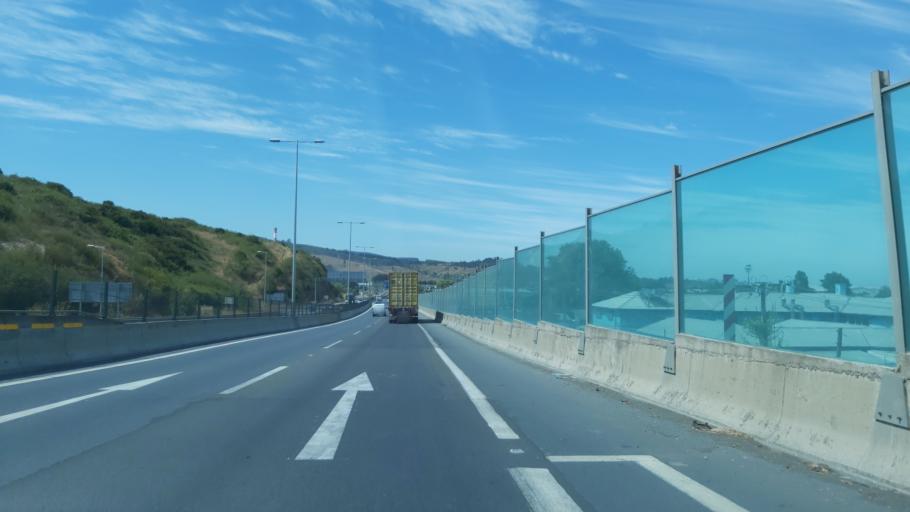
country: CL
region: Biobio
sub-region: Provincia de Concepcion
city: Coronel
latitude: -37.0277
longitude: -73.1352
